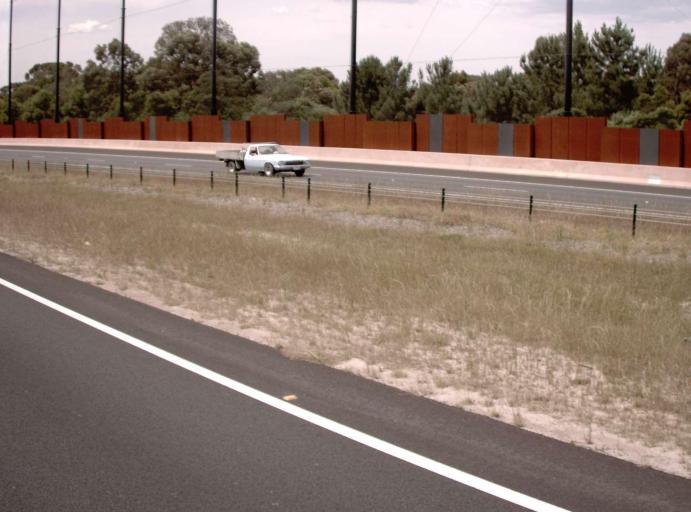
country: AU
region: Victoria
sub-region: Frankston
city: Frankston North
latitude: -38.1258
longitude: 145.1723
